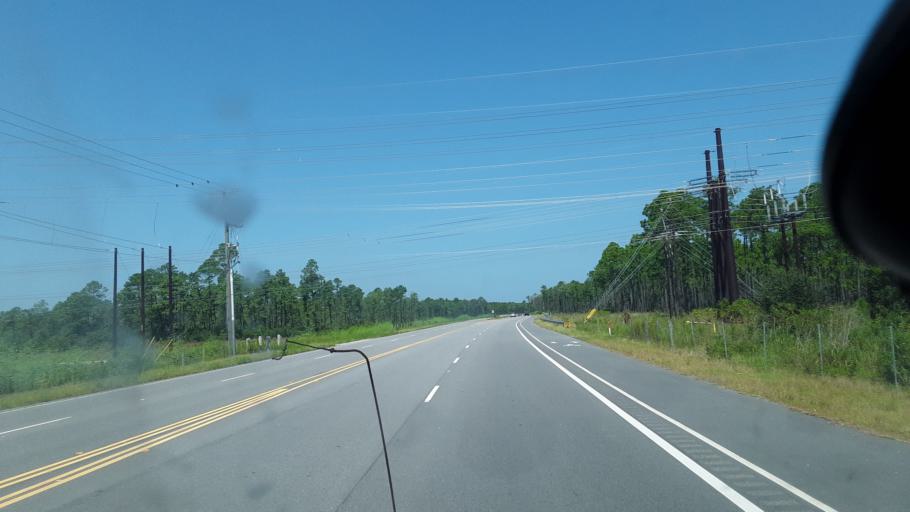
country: US
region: South Carolina
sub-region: Horry County
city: Myrtle Beach
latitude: 33.7857
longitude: -78.8777
